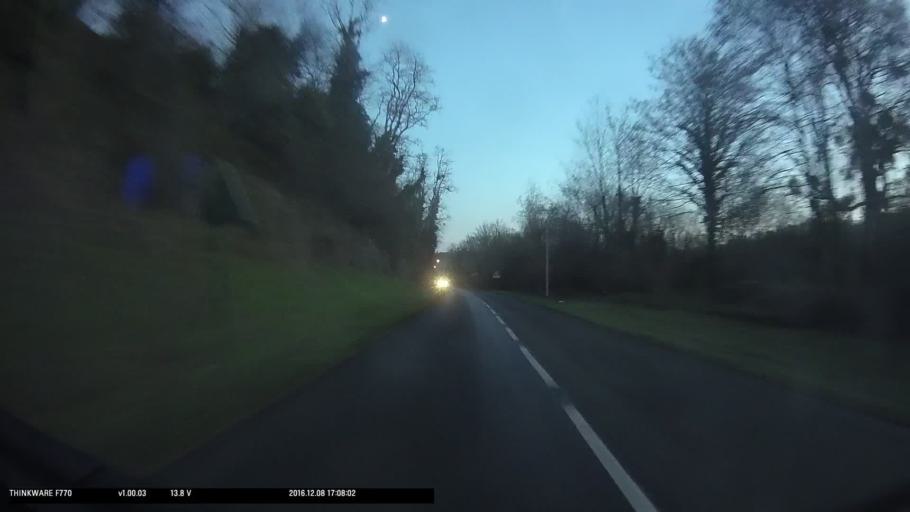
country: FR
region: Ile-de-France
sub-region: Departement du Val-d'Oise
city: Ableiges
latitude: 49.0830
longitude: 2.0000
